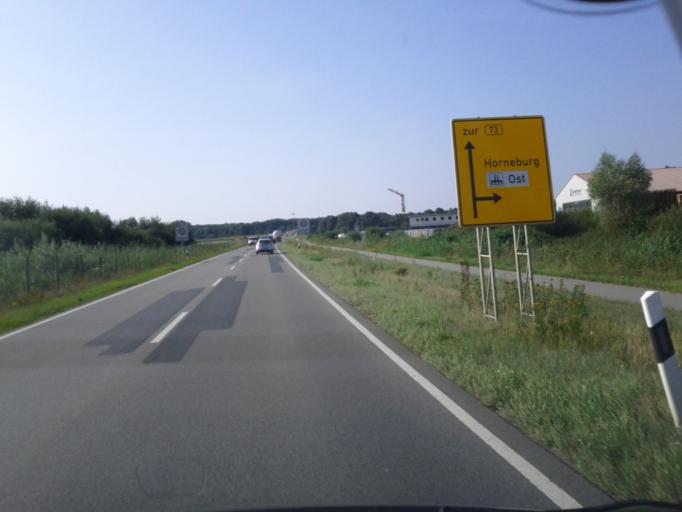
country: DE
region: Lower Saxony
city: Neuenkirchen
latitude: 53.5051
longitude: 9.5963
